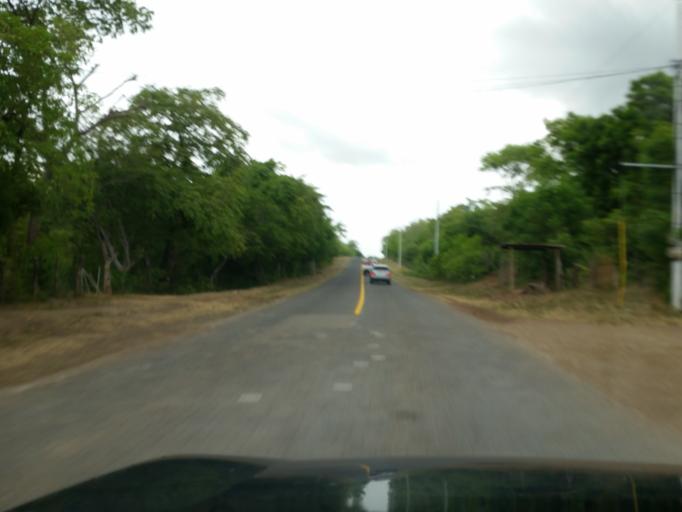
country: NI
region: Managua
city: Carlos Fonseca Amador
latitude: 11.9271
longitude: -86.5056
